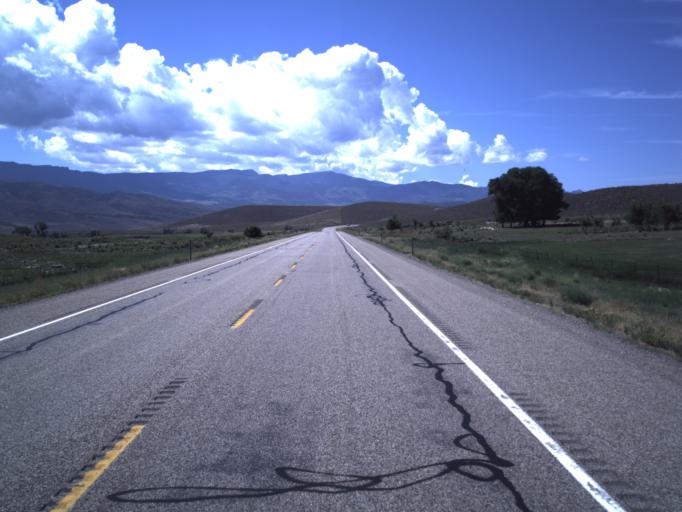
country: US
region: Utah
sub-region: Piute County
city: Junction
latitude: 38.2264
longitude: -112.2198
